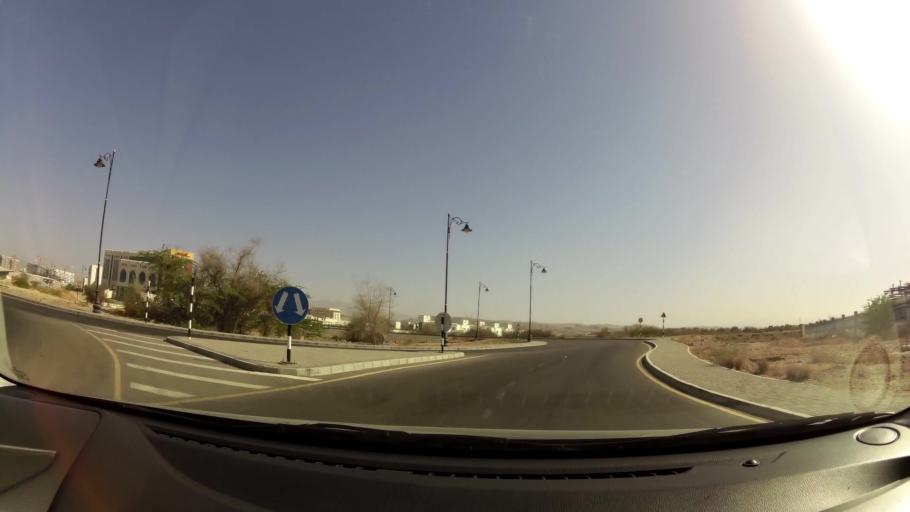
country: OM
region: Muhafazat Masqat
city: Bawshar
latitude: 23.5824
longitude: 58.2920
